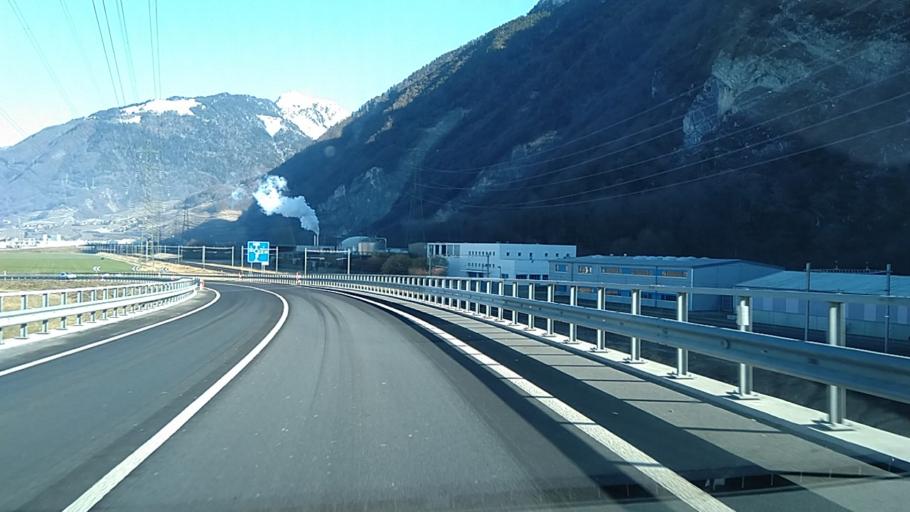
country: CH
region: Vaud
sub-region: Aigle District
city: Villeneuve
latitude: 46.3709
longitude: 6.9245
